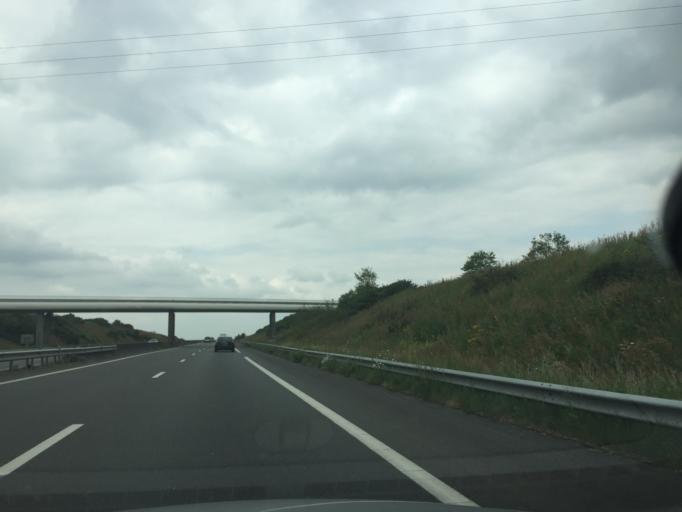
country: FR
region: Pays de la Loire
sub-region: Departement de la Loire-Atlantique
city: La Planche
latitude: 47.0380
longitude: -1.4092
